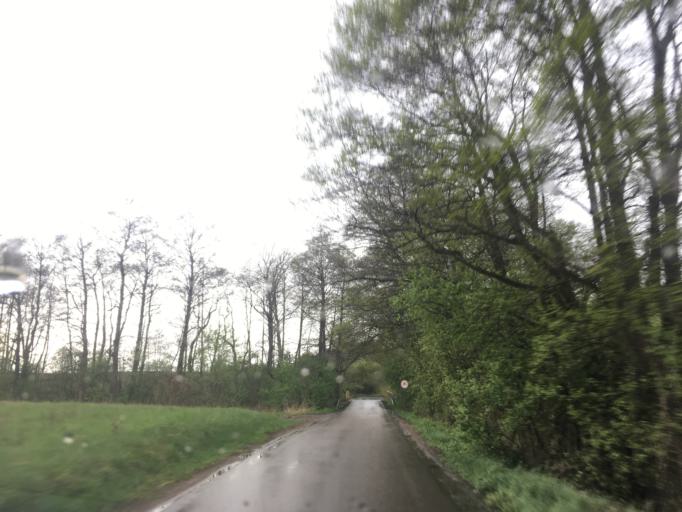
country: PL
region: Warmian-Masurian Voivodeship
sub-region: Powiat dzialdowski
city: Rybno
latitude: 53.3824
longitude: 19.9876
